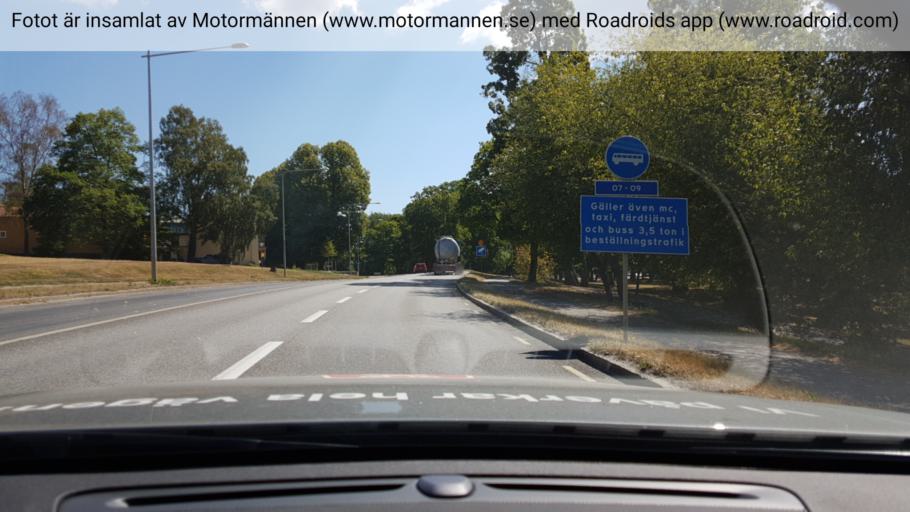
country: SE
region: Stockholm
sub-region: Stockholms Kommun
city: Bromma
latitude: 59.3253
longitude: 17.8842
